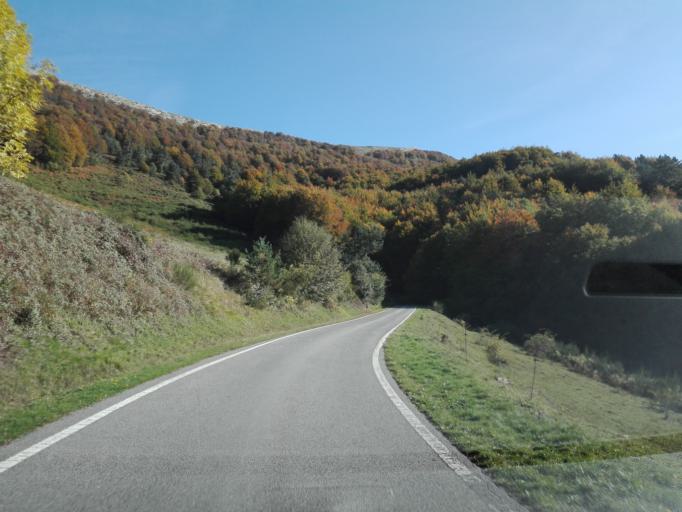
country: ES
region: Navarre
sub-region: Provincia de Navarra
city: Oronz
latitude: 42.9511
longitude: -1.1168
